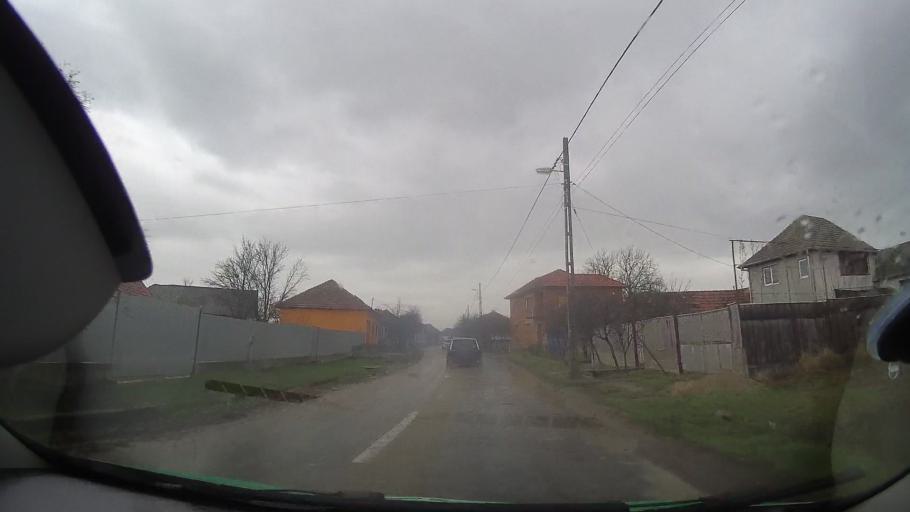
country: RO
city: Capalna
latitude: 46.7077
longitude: 22.0840
